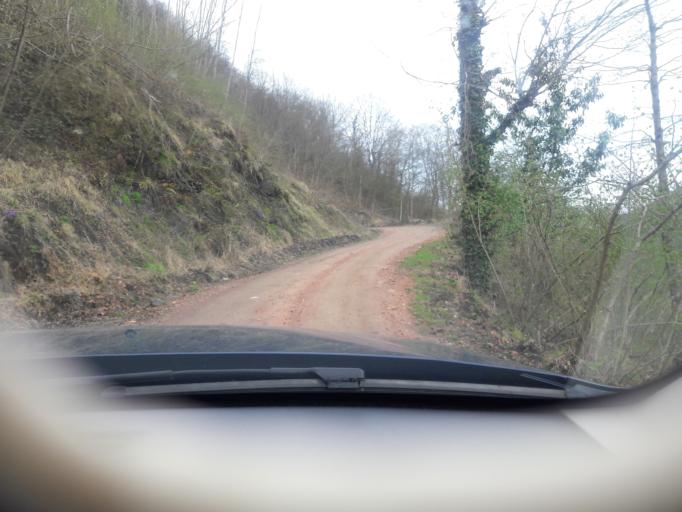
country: TR
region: Trabzon
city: Salpazari
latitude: 40.9717
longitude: 39.1969
